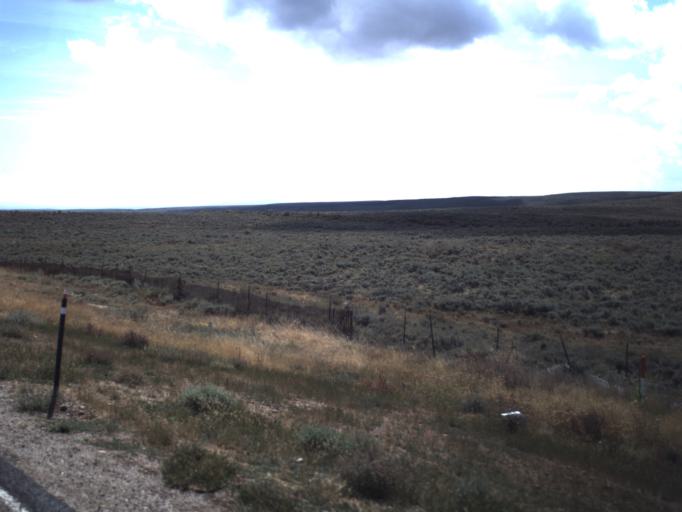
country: US
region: Utah
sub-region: Rich County
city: Randolph
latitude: 41.8027
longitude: -111.2454
